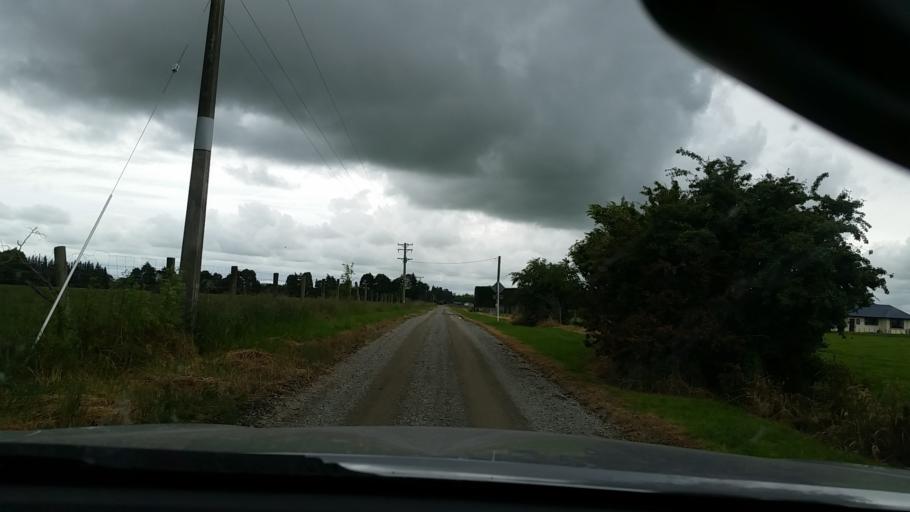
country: NZ
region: Southland
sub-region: Southland District
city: Winton
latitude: -46.0850
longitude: 168.3332
